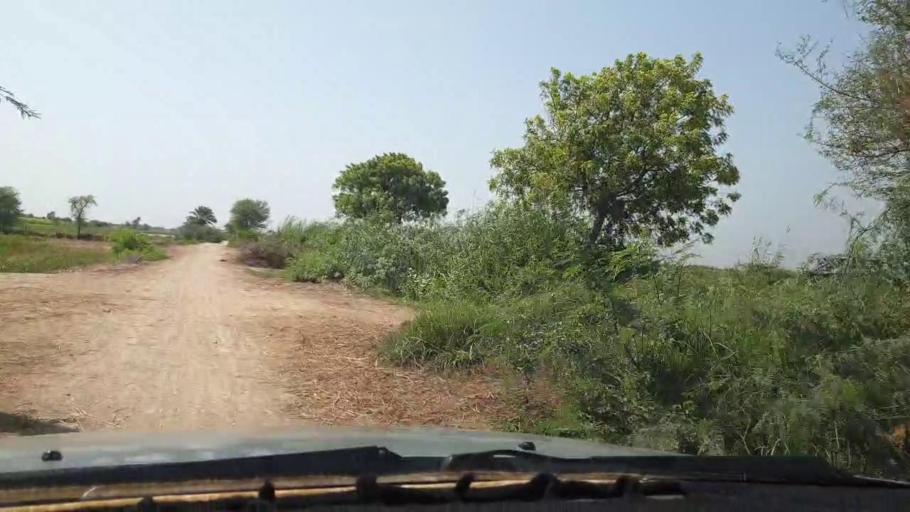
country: PK
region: Sindh
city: Tando Ghulam Ali
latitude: 25.1435
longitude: 68.7824
